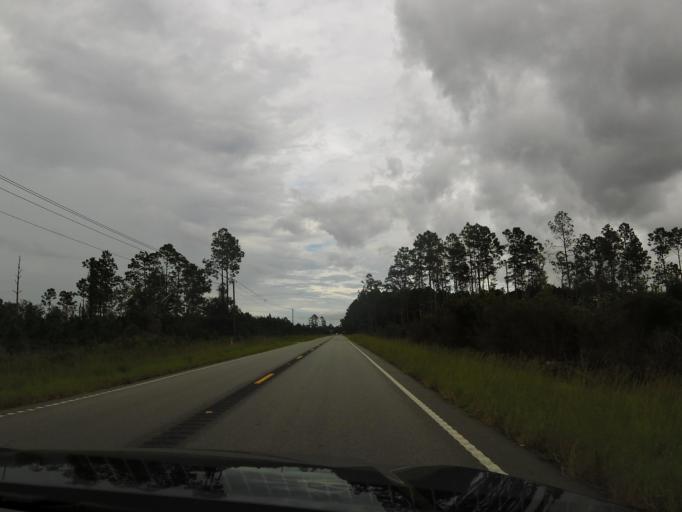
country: US
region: Florida
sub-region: Baker County
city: Macclenny
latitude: 30.5174
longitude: -82.1033
